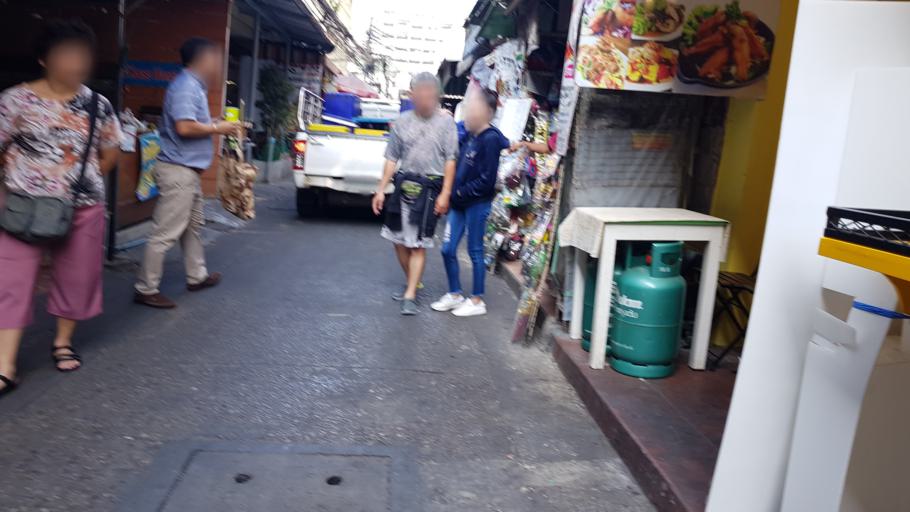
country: TH
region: Bangkok
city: Bangkok Noi
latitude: 13.7545
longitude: 100.4862
